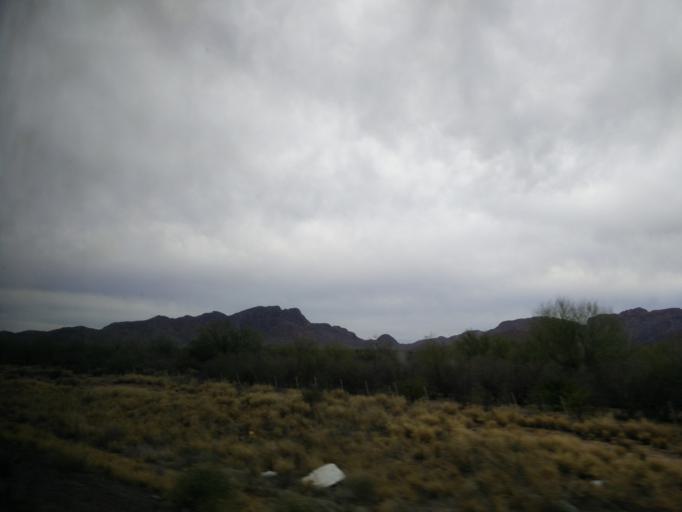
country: MX
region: Sonora
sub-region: Hermosillo
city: Miguel Aleman (La Doce)
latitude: 28.5729
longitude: -111.0311
